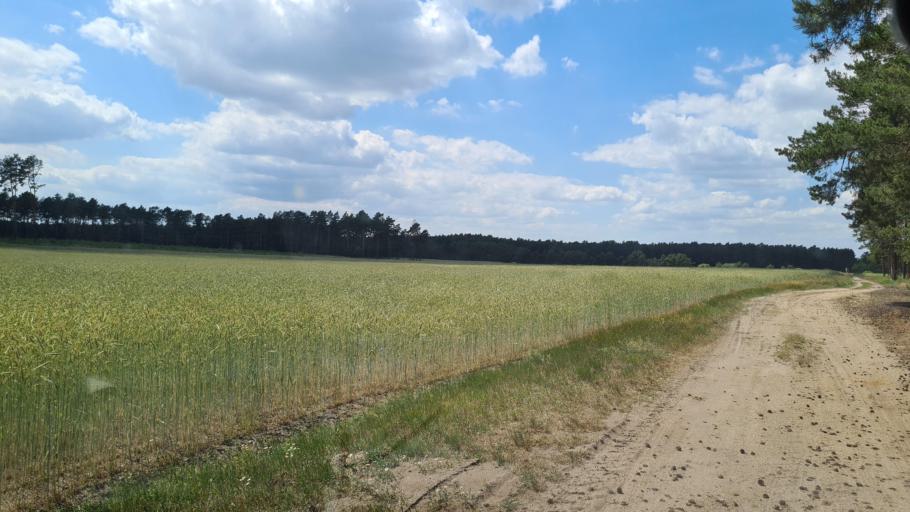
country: DE
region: Brandenburg
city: Sallgast
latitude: 51.6520
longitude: 13.8191
